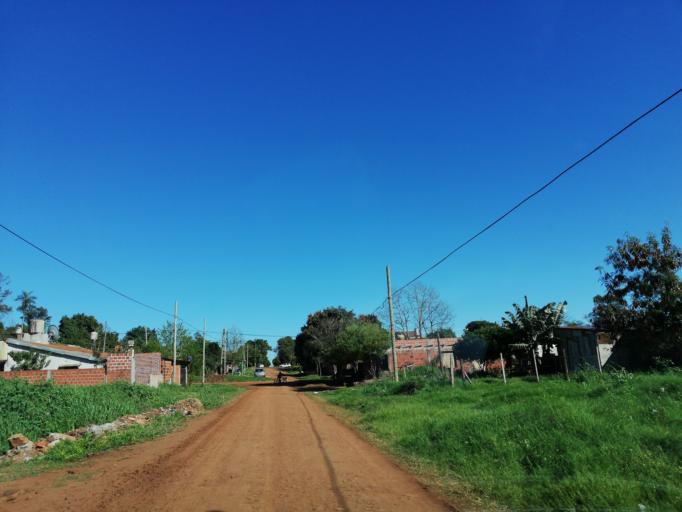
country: AR
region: Misiones
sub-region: Departamento de Capital
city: Posadas
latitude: -27.3954
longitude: -55.9302
